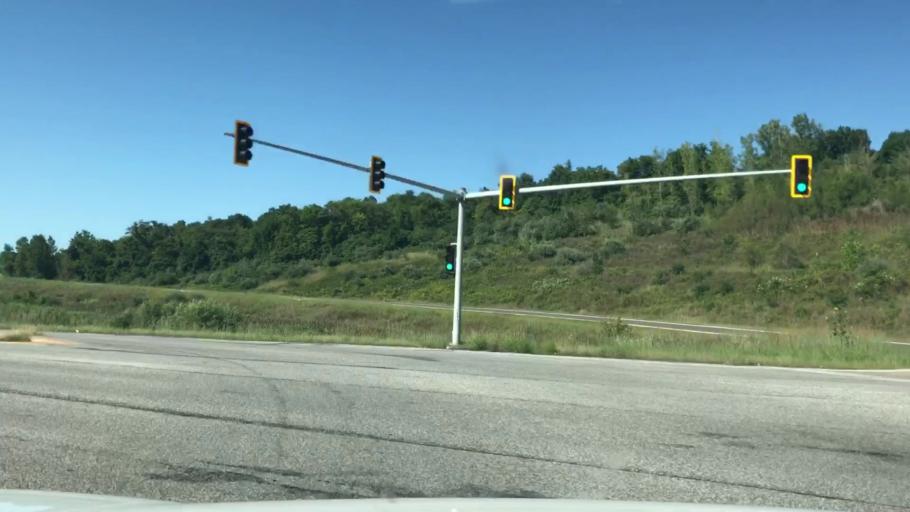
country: US
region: Illinois
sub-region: Madison County
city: South Roxana
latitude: 38.8492
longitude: -90.0495
